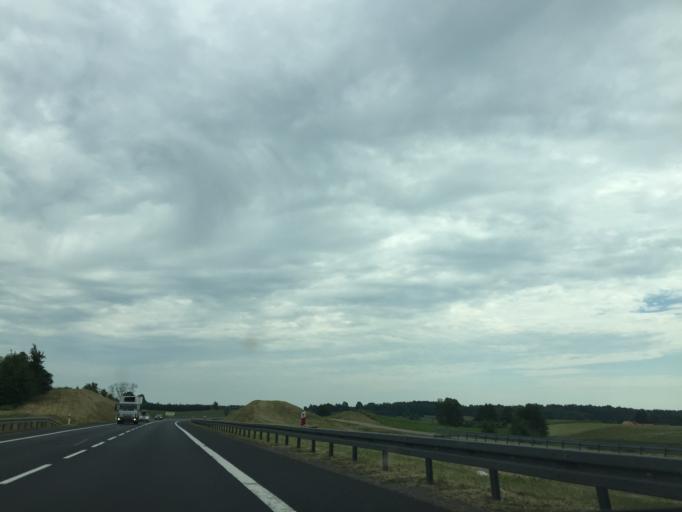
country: PL
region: Warmian-Masurian Voivodeship
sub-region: Powiat olsztynski
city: Biskupiec
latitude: 53.8318
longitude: 20.9023
